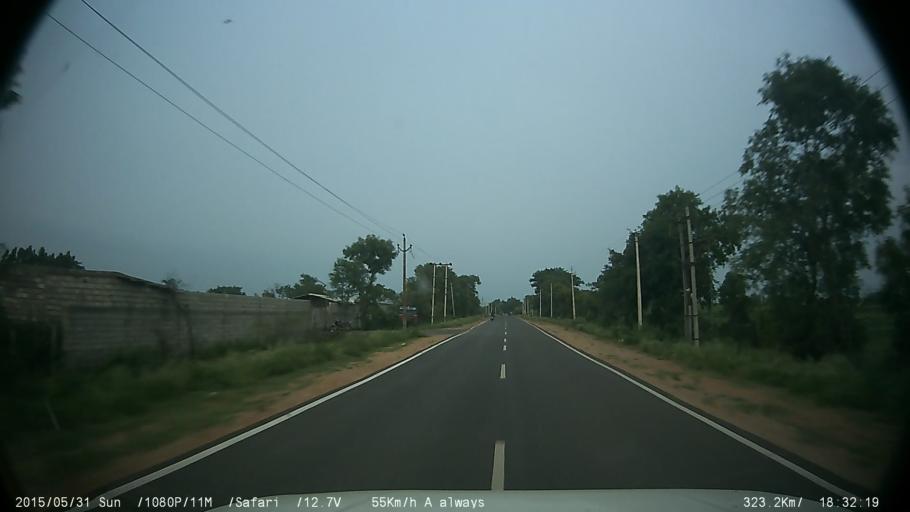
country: IN
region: Karnataka
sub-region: Mysore
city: Nanjangud
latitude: 12.1334
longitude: 76.7464
